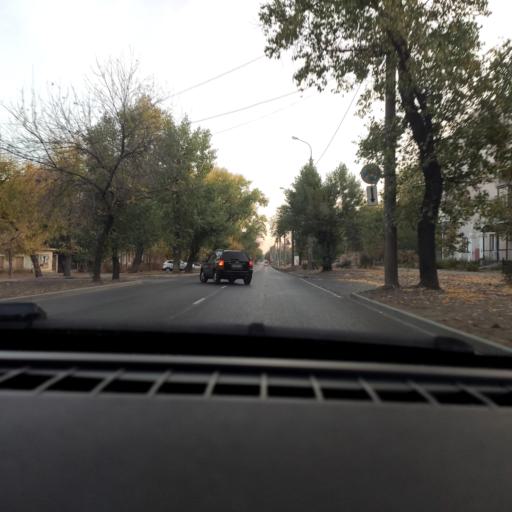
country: RU
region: Voronezj
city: Voronezh
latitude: 51.6397
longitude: 39.2397
